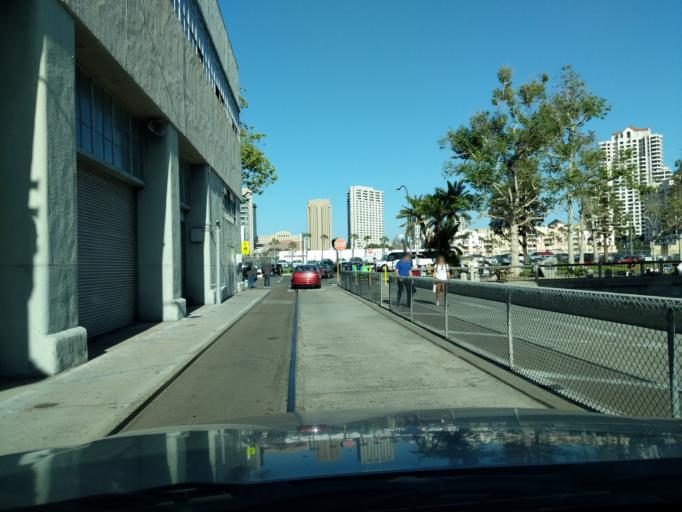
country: US
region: California
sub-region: San Diego County
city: San Diego
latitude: 32.7142
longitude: -117.1739
